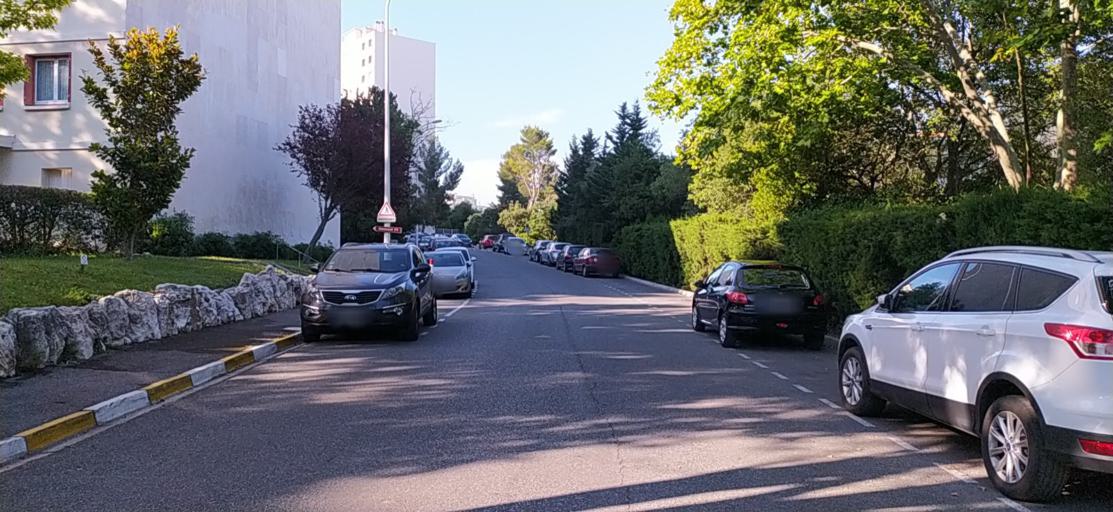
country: FR
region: Provence-Alpes-Cote d'Azur
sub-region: Departement des Bouches-du-Rhone
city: Marseille 09
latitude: 43.2500
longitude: 5.4166
